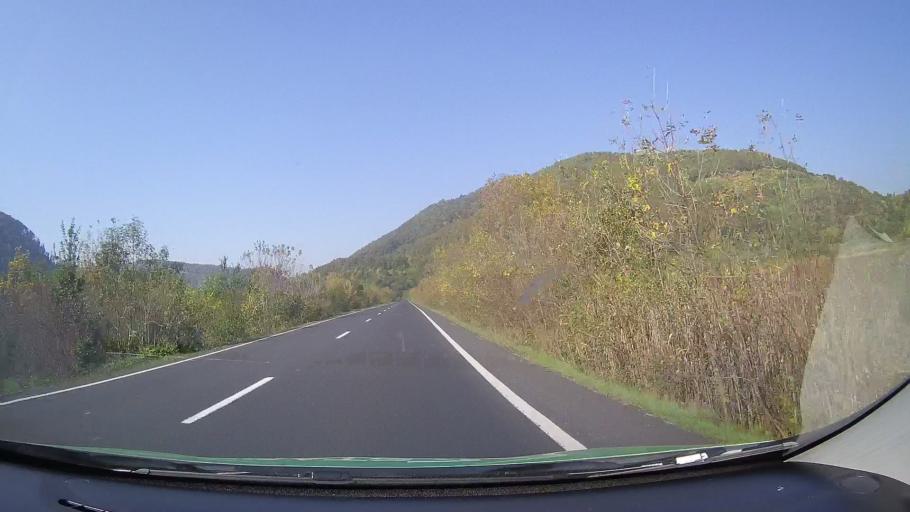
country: RO
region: Hunedoara
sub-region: Comuna Zam
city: Zam
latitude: 45.9720
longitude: 22.4579
